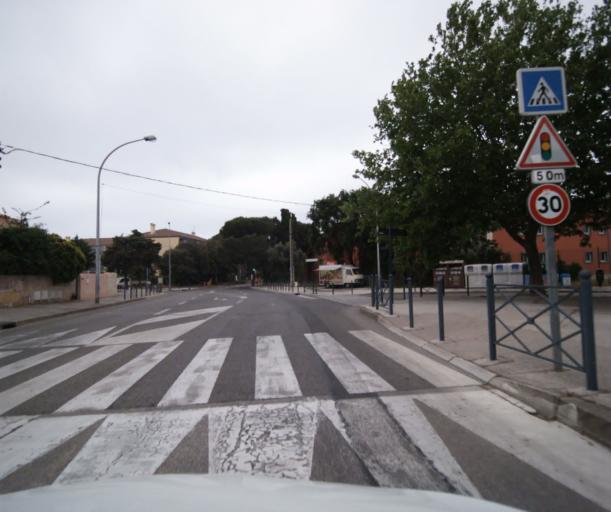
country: FR
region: Provence-Alpes-Cote d'Azur
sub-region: Departement du Var
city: La Seyne-sur-Mer
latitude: 43.0848
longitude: 5.8914
